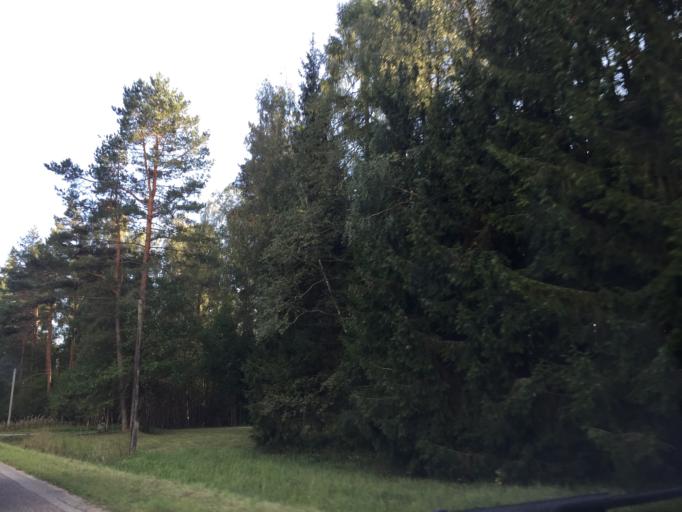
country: LV
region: Krimulda
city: Ragana
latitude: 57.2048
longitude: 24.7023
